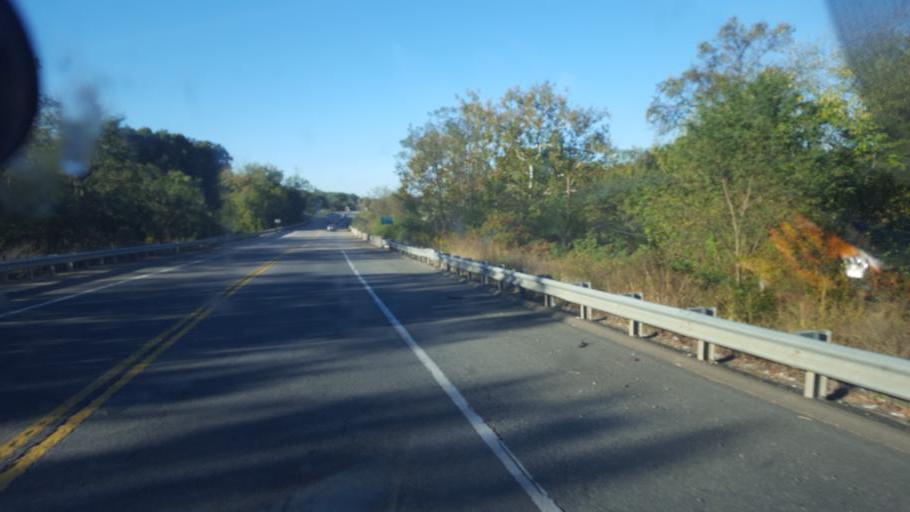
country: US
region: Virginia
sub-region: Prince William County
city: Nokesville
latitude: 38.6494
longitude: -77.6471
